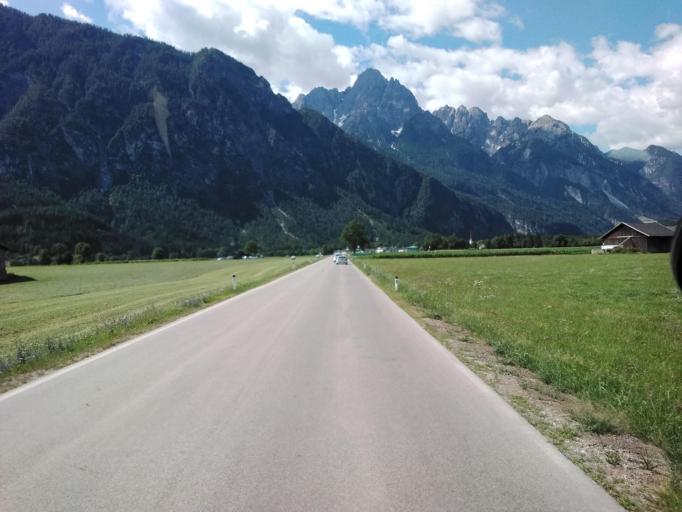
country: AT
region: Tyrol
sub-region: Politischer Bezirk Lienz
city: Lienz
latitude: 46.8225
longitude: 12.7679
